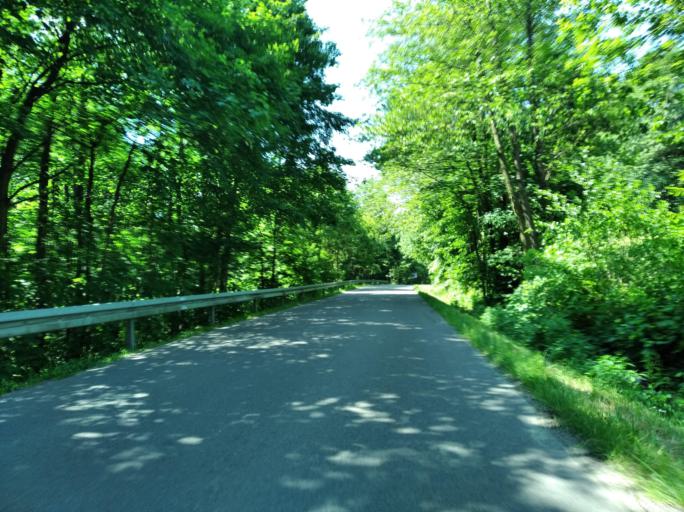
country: PL
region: Subcarpathian Voivodeship
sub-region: Powiat ropczycko-sedziszowski
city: Zagorzyce
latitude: 49.9816
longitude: 21.6465
